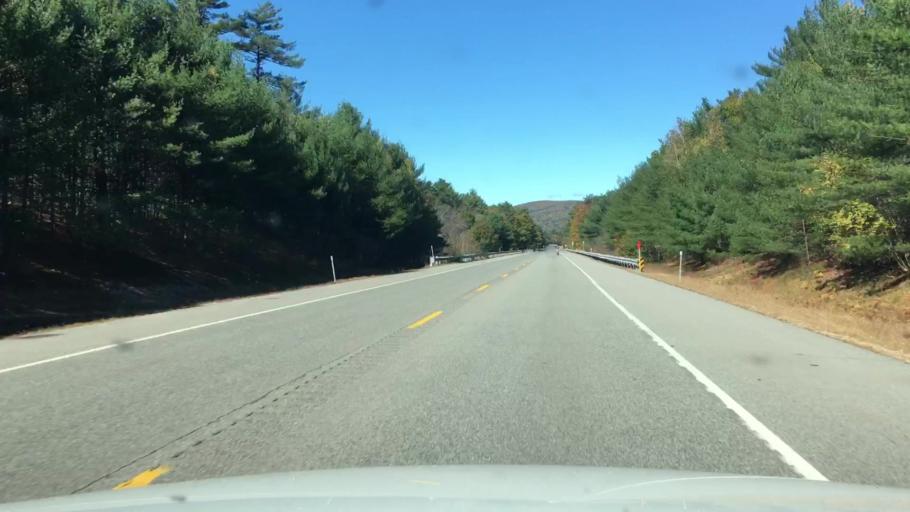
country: US
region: New Hampshire
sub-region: Carroll County
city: Sanbornville
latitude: 43.4889
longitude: -71.0129
